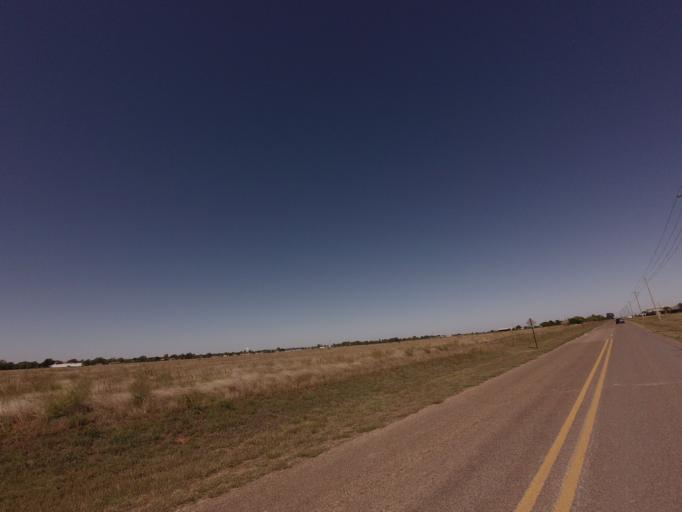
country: US
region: New Mexico
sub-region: Curry County
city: Clovis
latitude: 34.4199
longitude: -103.1608
